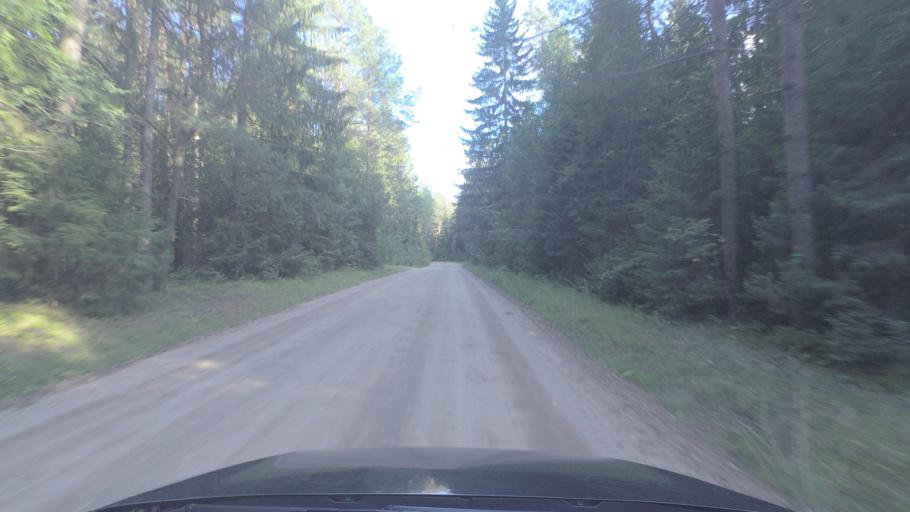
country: LT
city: Svencioneliai
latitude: 55.1656
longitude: 25.8413
